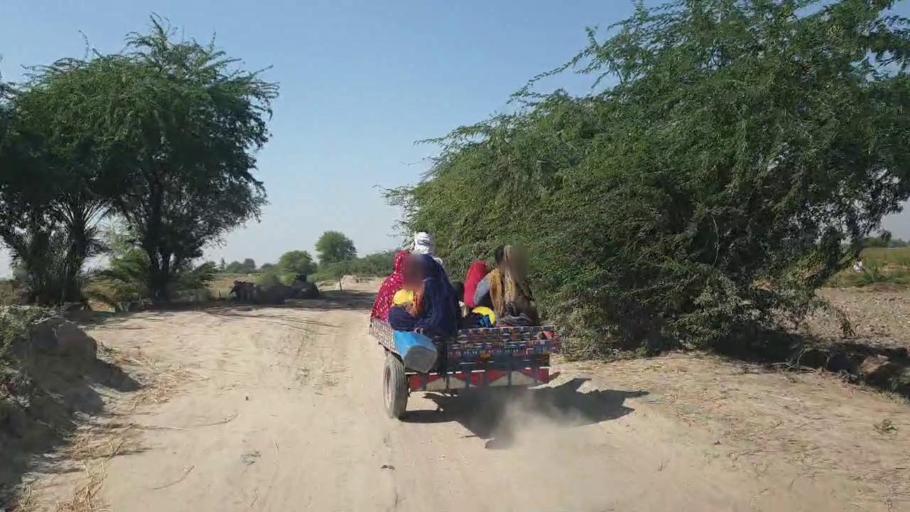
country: PK
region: Sindh
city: Talhar
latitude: 24.8339
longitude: 68.8137
